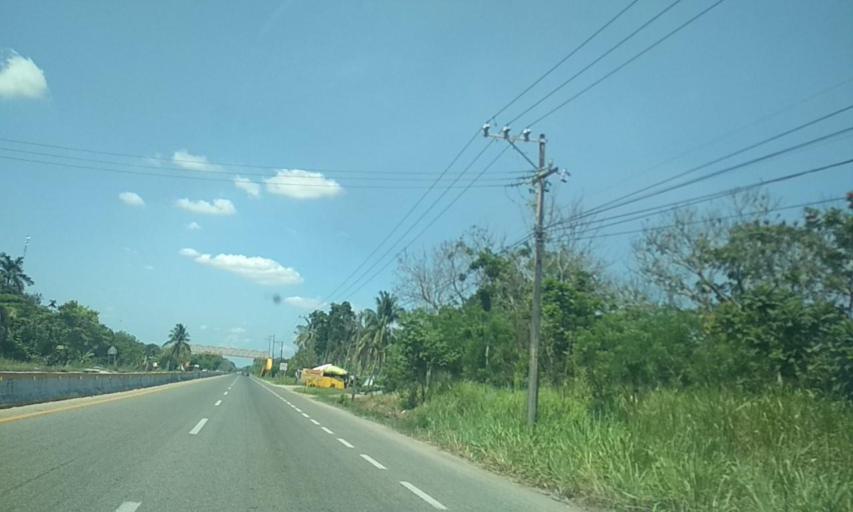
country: MX
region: Tabasco
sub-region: Huimanguillo
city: El Dorado
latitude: 17.8669
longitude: -93.3822
